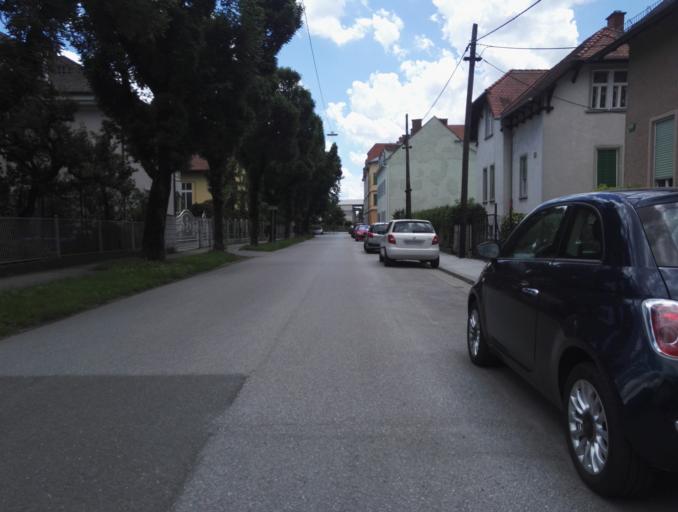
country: AT
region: Styria
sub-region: Graz Stadt
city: Wetzelsdorf
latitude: 47.0655
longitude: 15.4046
